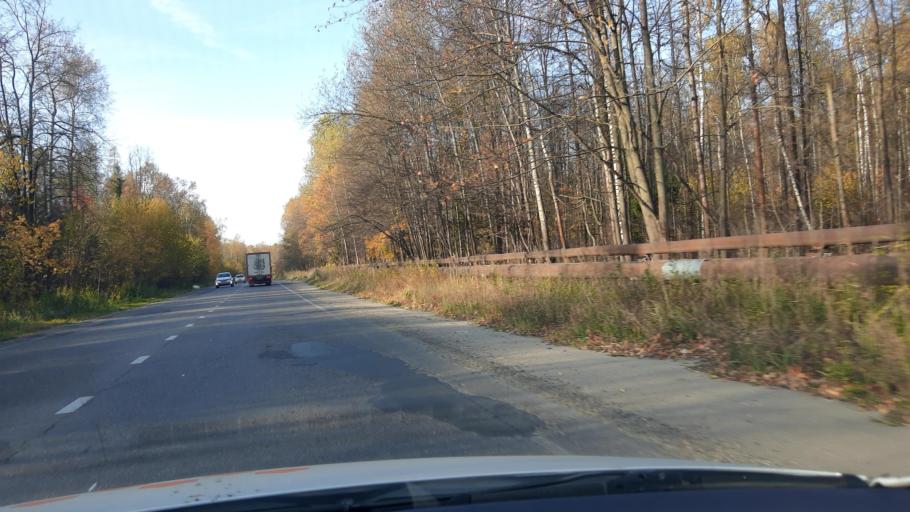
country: RU
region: Moskovskaya
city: Fryazevo
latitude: 55.7682
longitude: 38.4872
